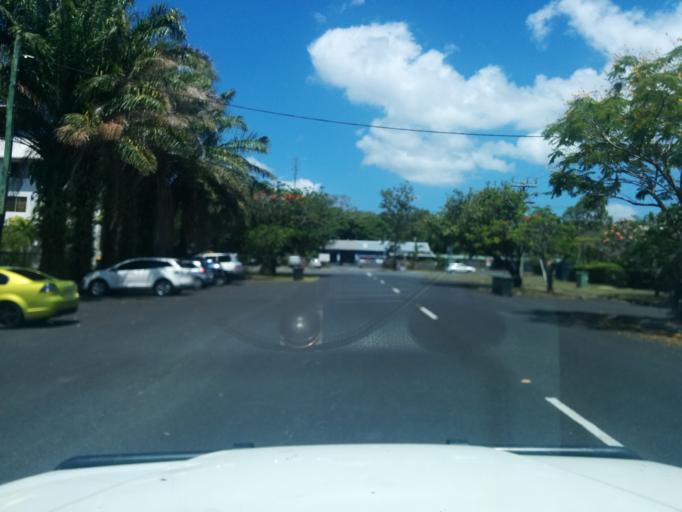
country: AU
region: Queensland
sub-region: Cairns
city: Cairns
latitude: -16.9120
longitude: 145.7492
